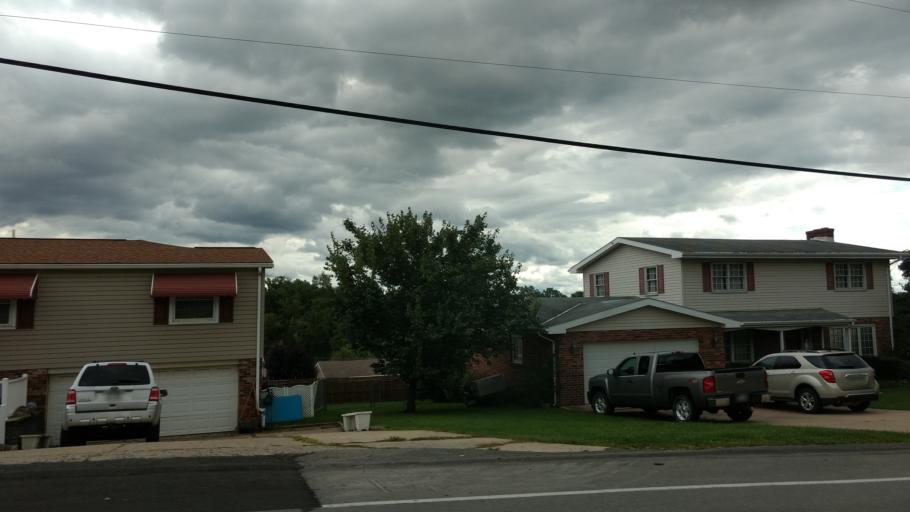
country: US
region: Pennsylvania
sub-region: Westmoreland County
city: Lynnwood-Pricedale
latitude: 40.1435
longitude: -79.8402
